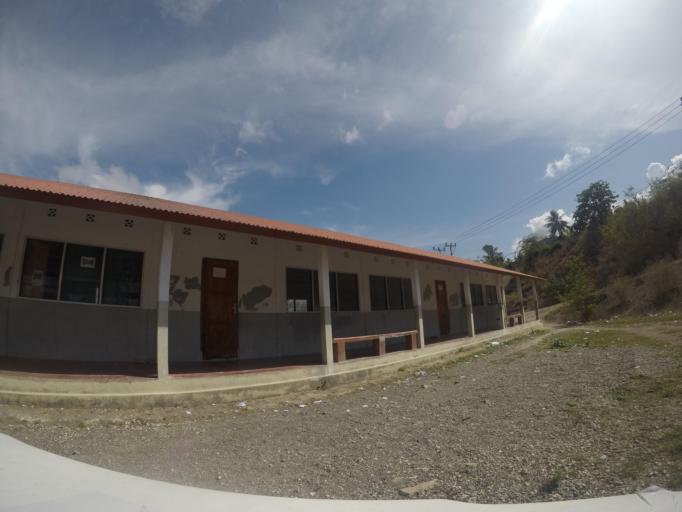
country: TL
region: Baucau
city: Baucau
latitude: -8.4667
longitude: 126.4721
